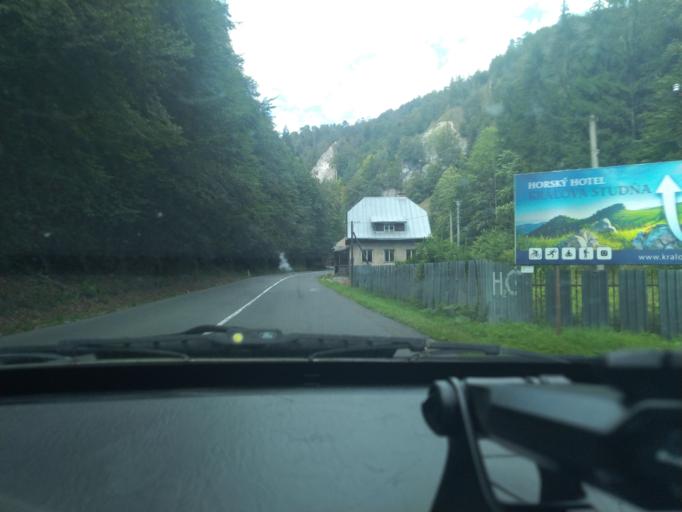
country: SK
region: Banskobystricky
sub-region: Okres Banska Bystrica
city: Banska Bystrica
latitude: 48.8190
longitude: 19.0380
